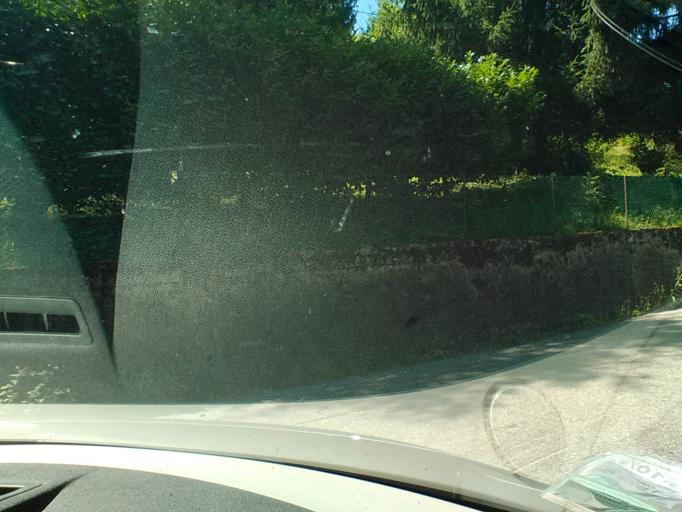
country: FR
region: Rhone-Alpes
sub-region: Departement de la Savoie
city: Chambery
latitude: 45.5595
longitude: 5.9309
